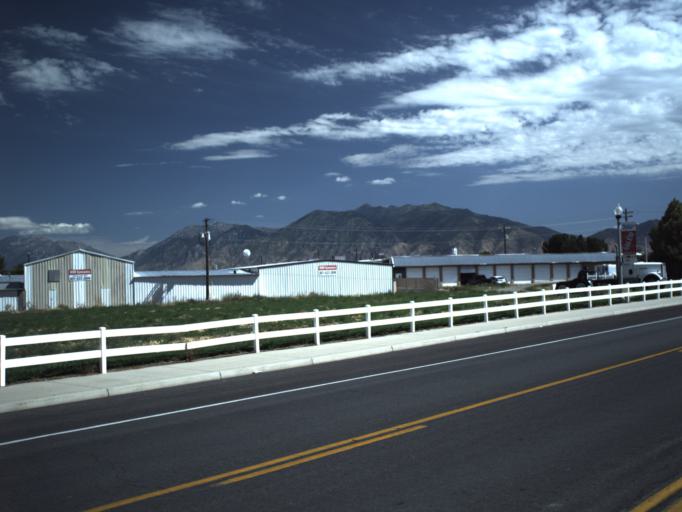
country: US
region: Utah
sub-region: Utah County
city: Salem
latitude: 40.0581
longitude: -111.6709
